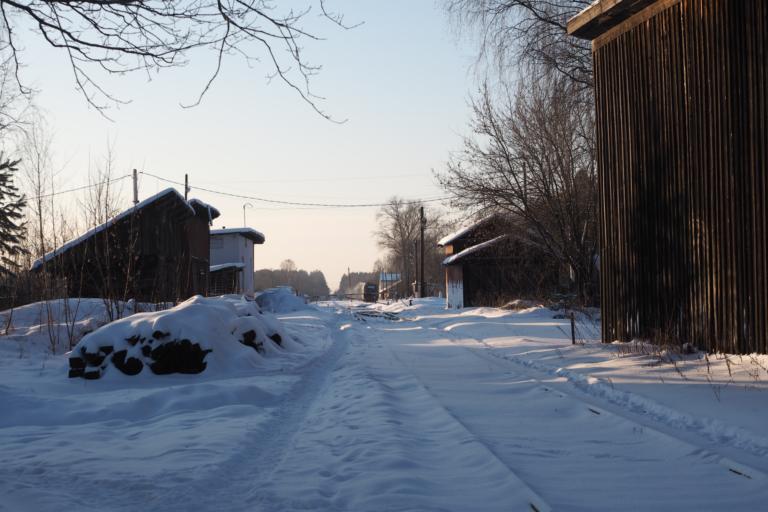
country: RU
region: Tverskaya
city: Ves'yegonsk
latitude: 58.6556
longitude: 37.2706
